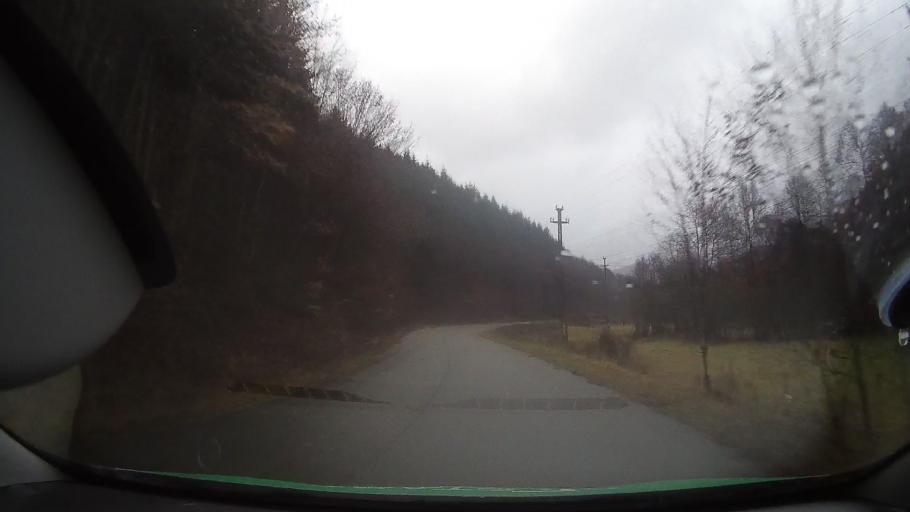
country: RO
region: Alba
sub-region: Comuna Avram Iancu
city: Avram Iancu
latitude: 46.2956
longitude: 22.7558
